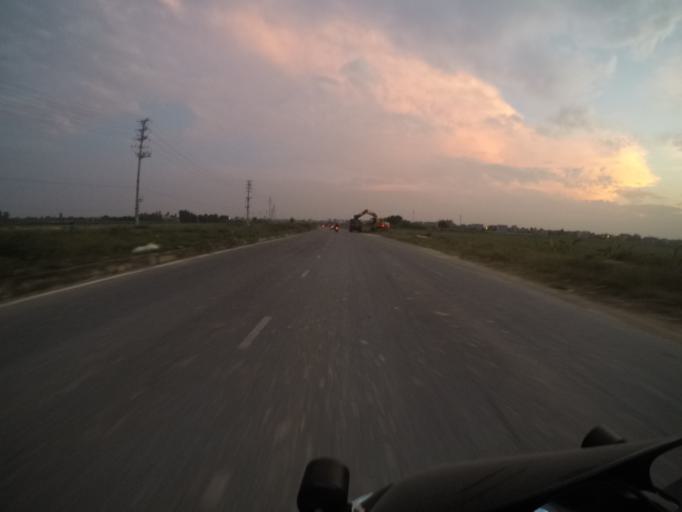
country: VN
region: Vinh Phuc
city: Phuc Yen
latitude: 21.2454
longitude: 105.7218
